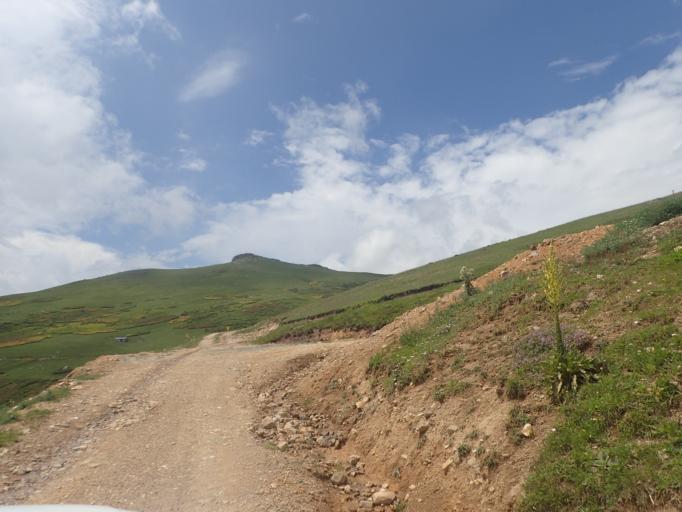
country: TR
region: Ordu
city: Yesilce
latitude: 40.5957
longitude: 37.9578
